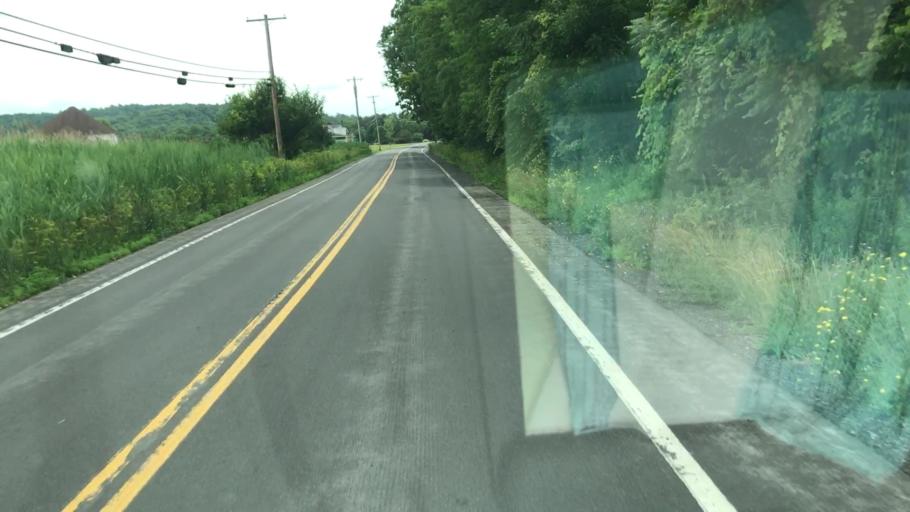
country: US
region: New York
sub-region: Onondaga County
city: Manlius
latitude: 42.9706
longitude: -75.9882
